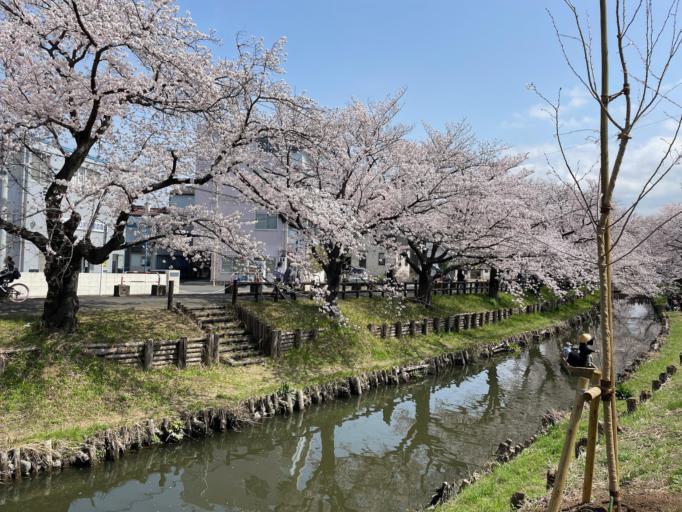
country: JP
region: Saitama
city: Kawagoe
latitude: 35.9288
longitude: 139.4871
